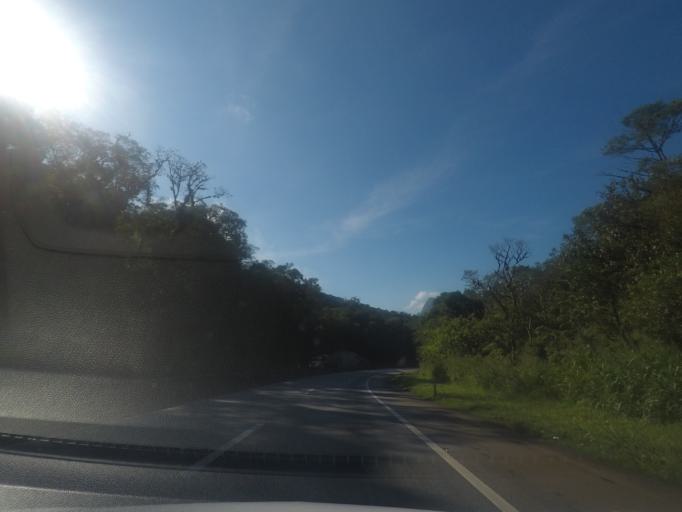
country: BR
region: Parana
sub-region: Piraquara
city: Piraquara
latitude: -25.5933
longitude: -48.9096
